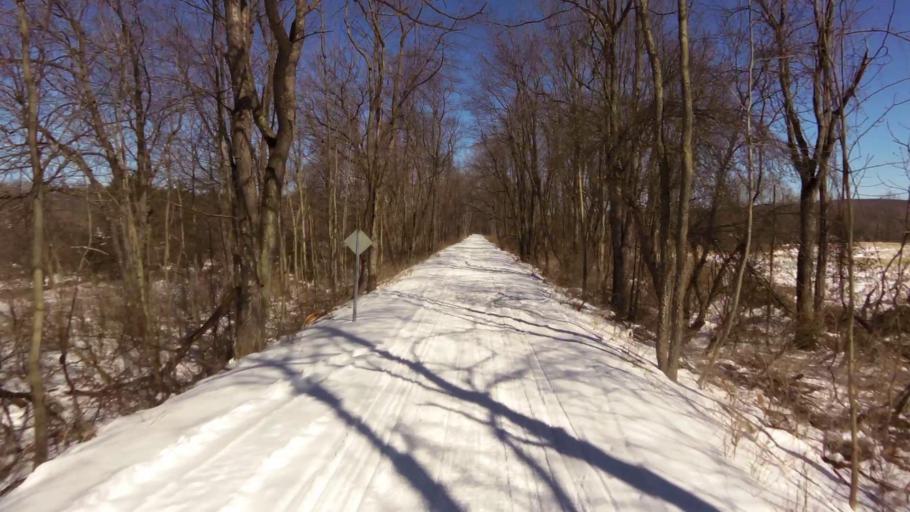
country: US
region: New York
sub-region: Allegany County
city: Houghton
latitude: 42.3493
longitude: -78.1255
